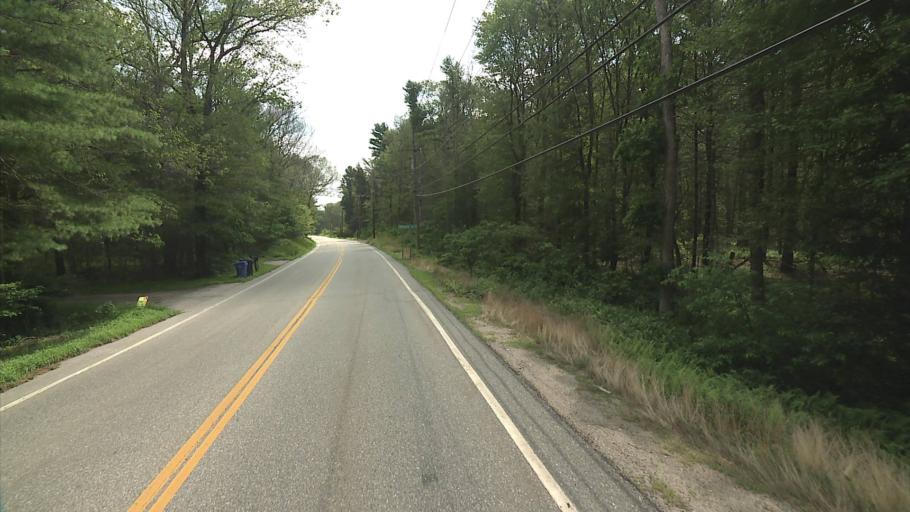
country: US
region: Rhode Island
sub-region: Washington County
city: Hopkinton
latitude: 41.5733
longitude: -71.8326
